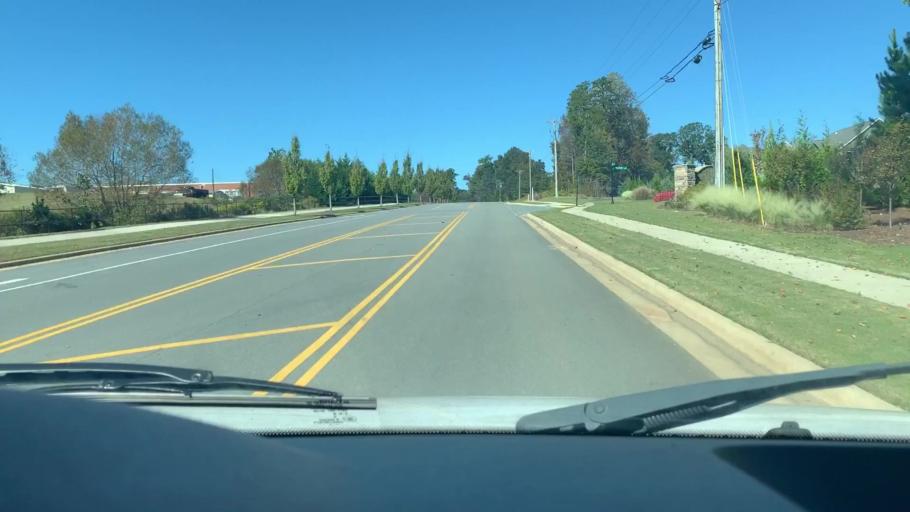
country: US
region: North Carolina
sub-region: Gaston County
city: Davidson
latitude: 35.4681
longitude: -80.8256
